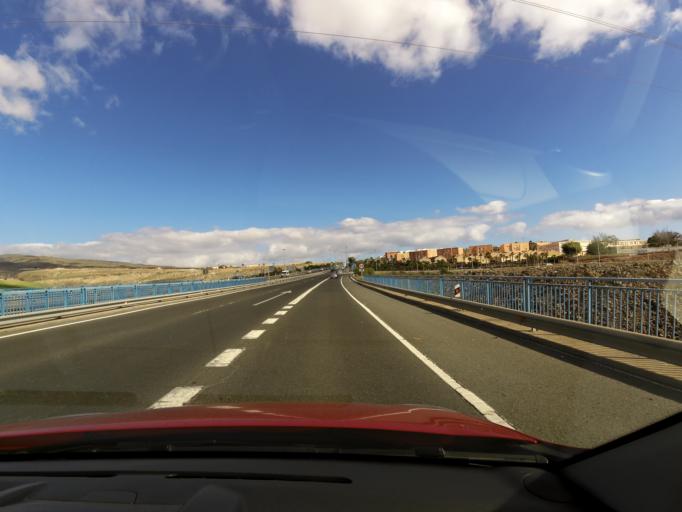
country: ES
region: Canary Islands
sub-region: Provincia de Las Palmas
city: Maspalomas
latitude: 27.7707
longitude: -15.5934
